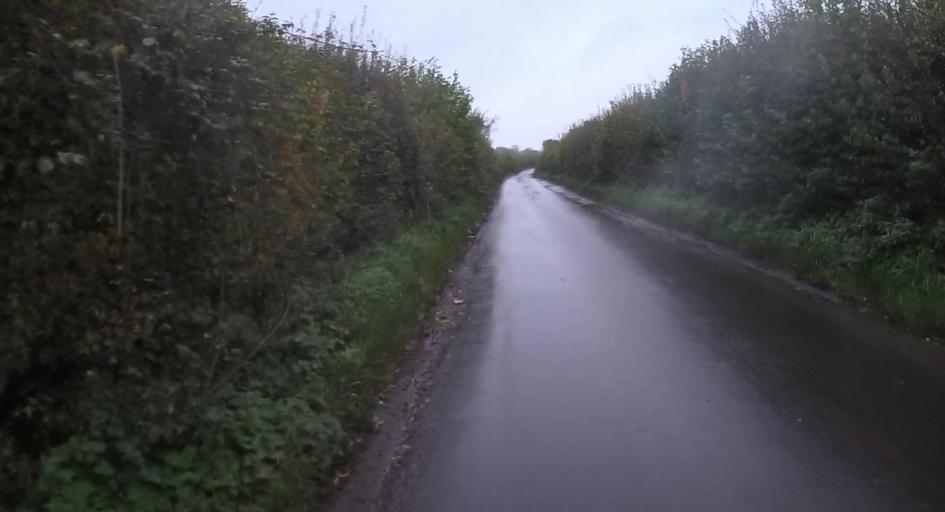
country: GB
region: England
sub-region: Surrey
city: Farnham
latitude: 51.2075
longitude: -0.8536
